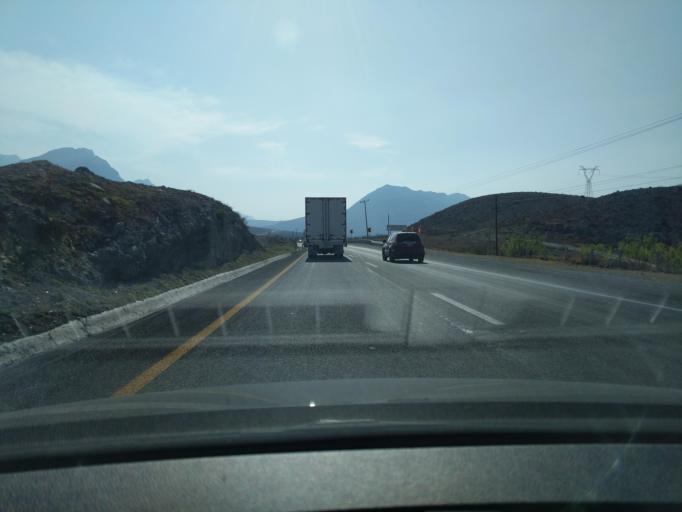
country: MX
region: Nuevo Leon
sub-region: Garcia
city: Las Torres de Guadalupe
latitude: 25.6764
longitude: -100.6776
